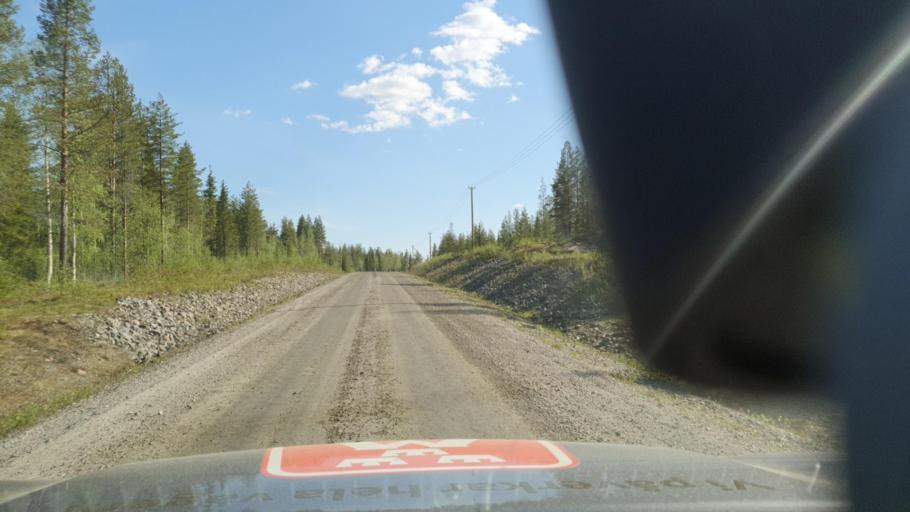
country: SE
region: Norrbotten
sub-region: Bodens Kommun
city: Boden
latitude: 66.4933
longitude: 21.9064
